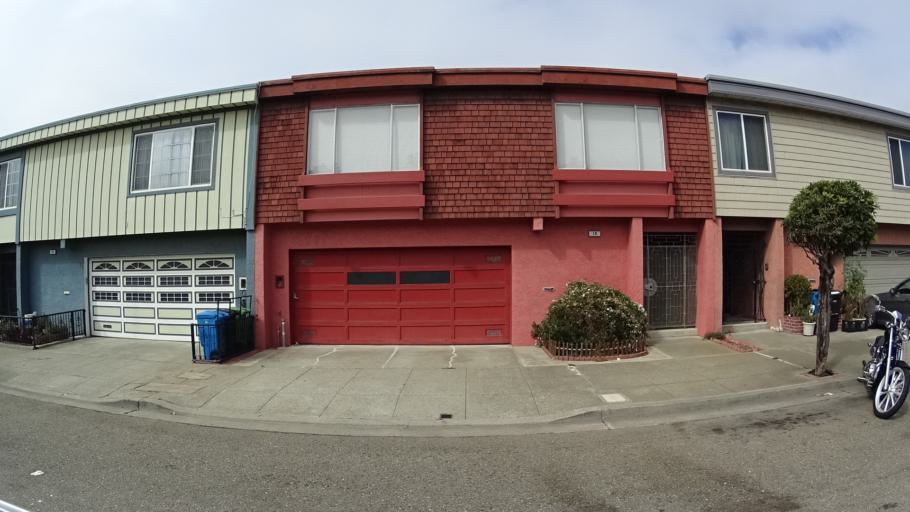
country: US
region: California
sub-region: San Mateo County
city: Daly City
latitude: 37.7097
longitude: -122.4439
